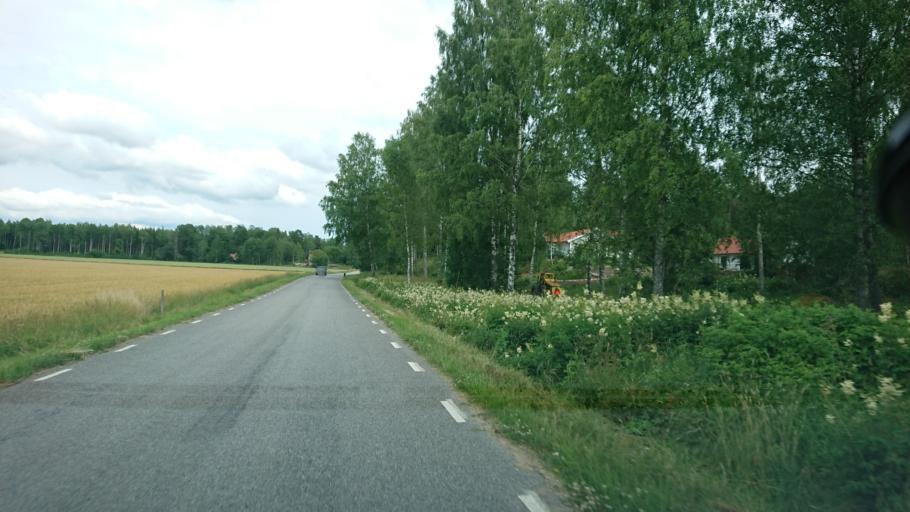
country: SE
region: Uppsala
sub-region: Osthammars Kommun
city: Bjorklinge
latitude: 60.0011
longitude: 17.4664
